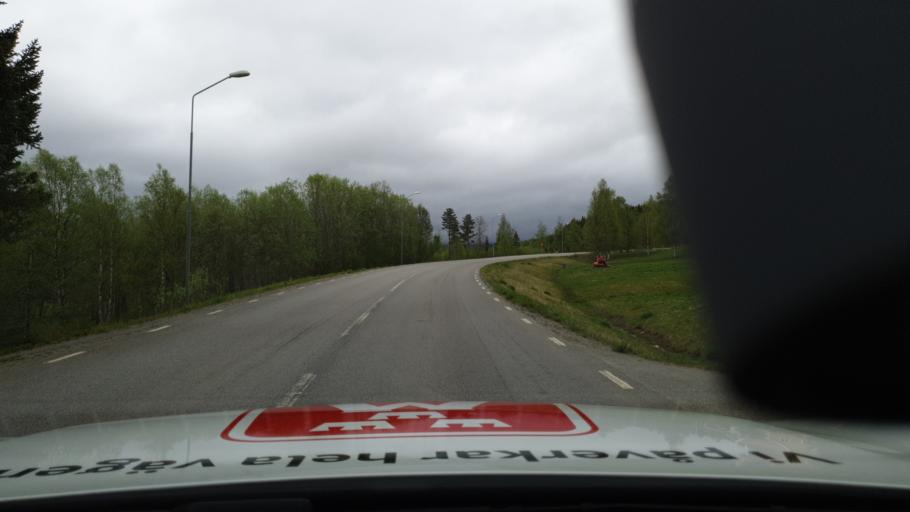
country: NO
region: Nord-Trondelag
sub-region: Lierne
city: Sandvika
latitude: 64.4945
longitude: 14.1402
